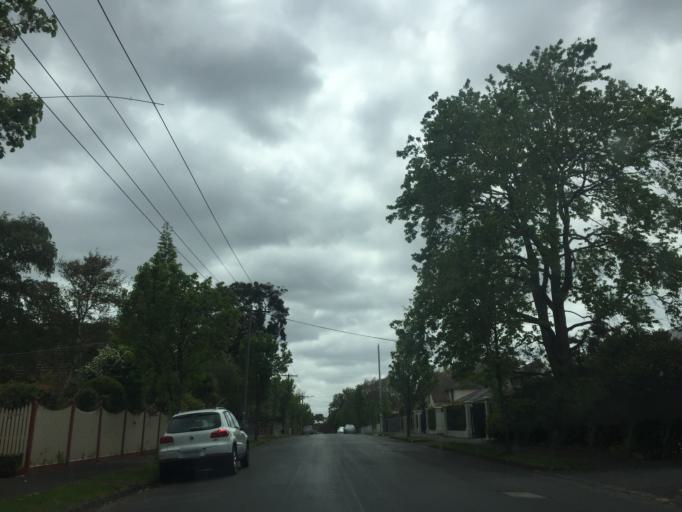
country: AU
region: Victoria
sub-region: Boroondara
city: Kew East
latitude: -37.8079
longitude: 145.0450
